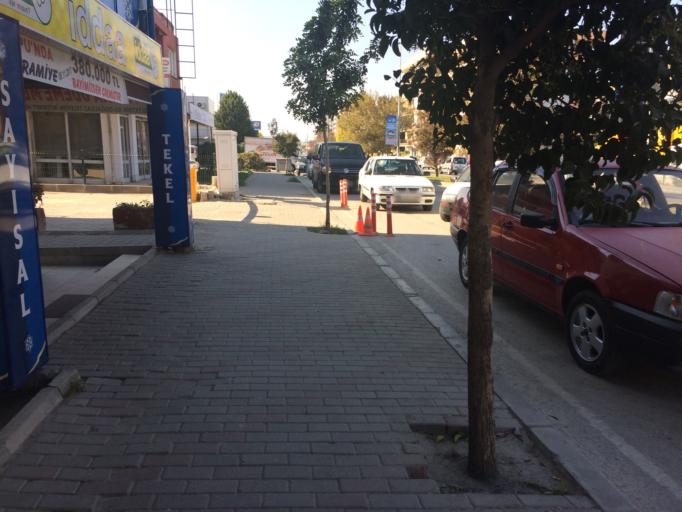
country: TR
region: Izmir
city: Karsiyaka
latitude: 38.4933
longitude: 27.0533
